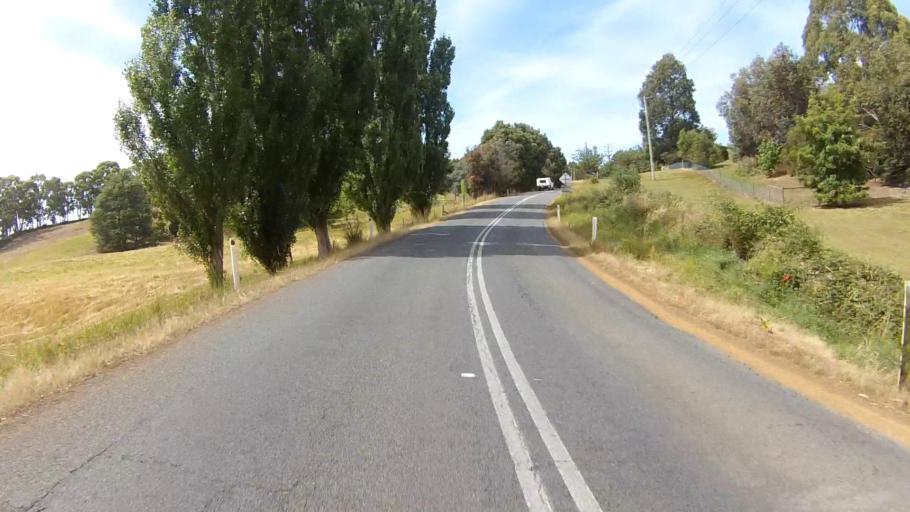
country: AU
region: Tasmania
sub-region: Kingborough
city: Kettering
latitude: -43.2086
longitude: 147.2556
